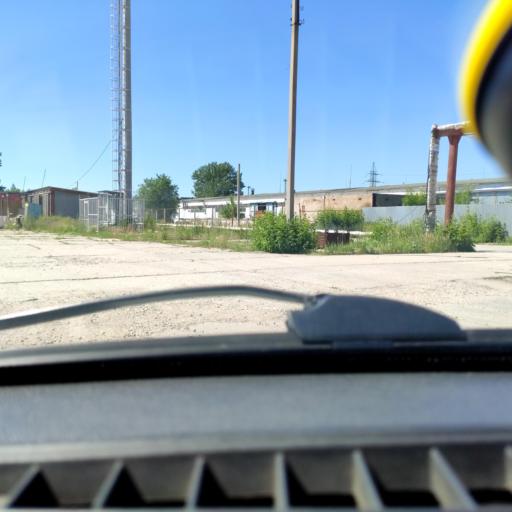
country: RU
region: Samara
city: Tol'yatti
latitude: 53.5725
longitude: 49.3021
